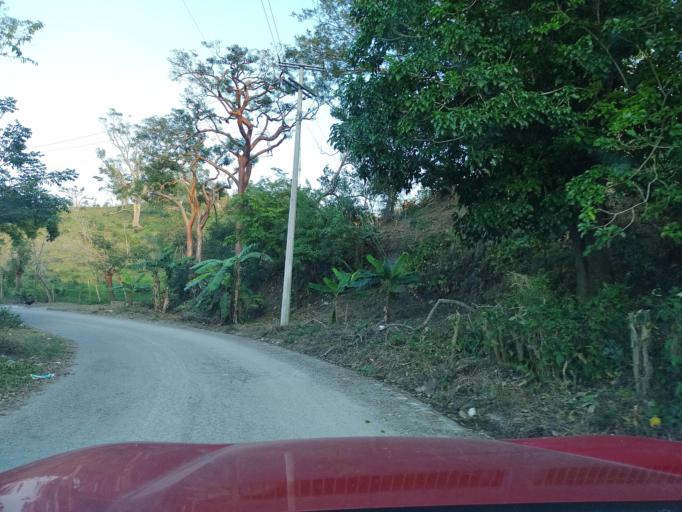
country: MX
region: Veracruz
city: Agua Dulce
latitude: 20.4041
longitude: -97.2858
